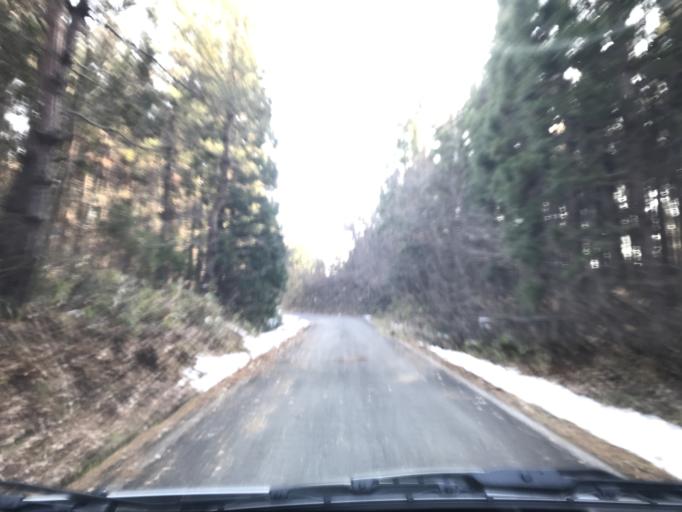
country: JP
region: Iwate
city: Ichinoseki
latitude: 38.9753
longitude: 141.0420
